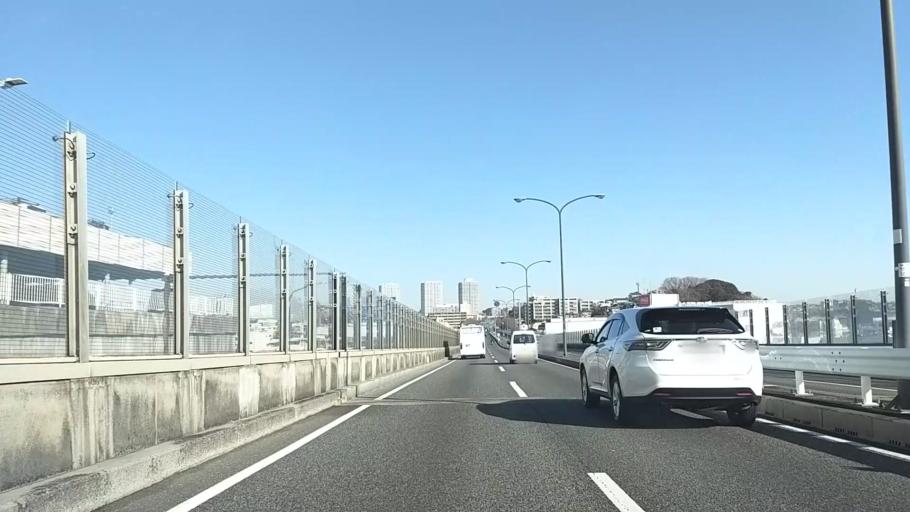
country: JP
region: Kanagawa
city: Yokohama
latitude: 35.4168
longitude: 139.5593
